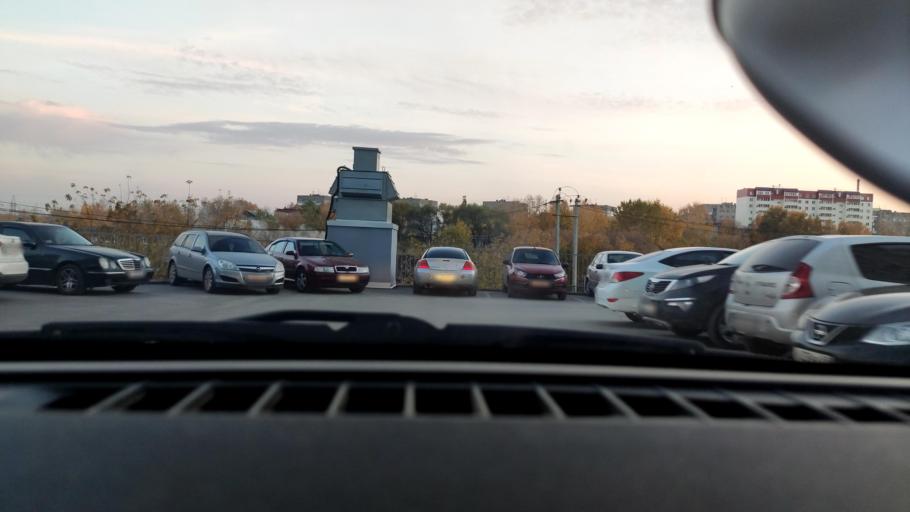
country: RU
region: Perm
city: Perm
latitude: 57.9898
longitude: 56.2683
